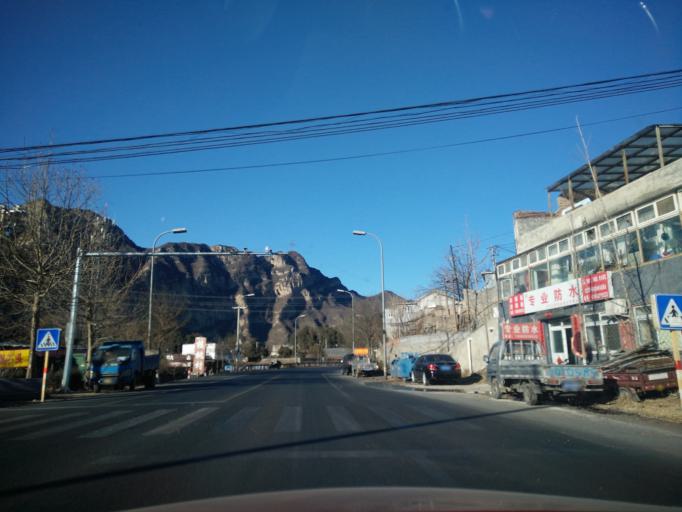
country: CN
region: Beijing
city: Miaofengshan
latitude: 39.9757
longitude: 116.0443
